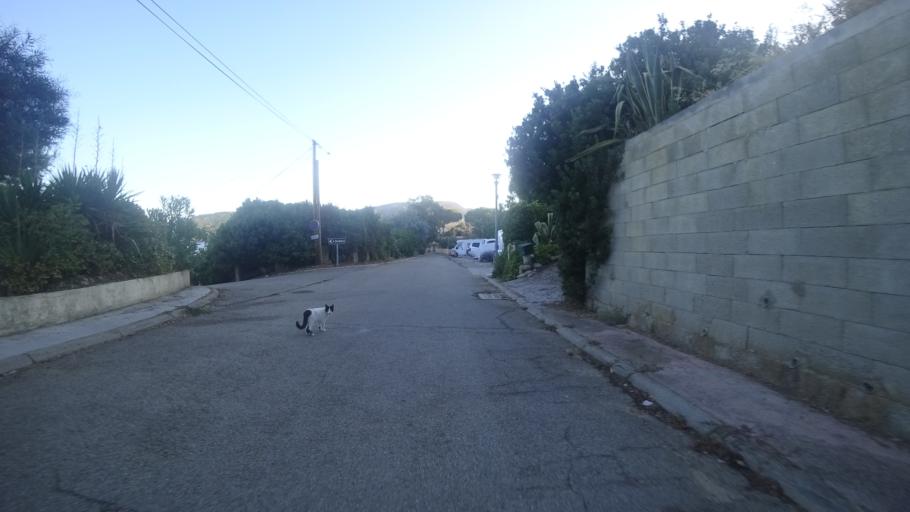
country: FR
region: Corsica
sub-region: Departement de la Corse-du-Sud
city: Alata
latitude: 41.9786
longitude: 8.6667
